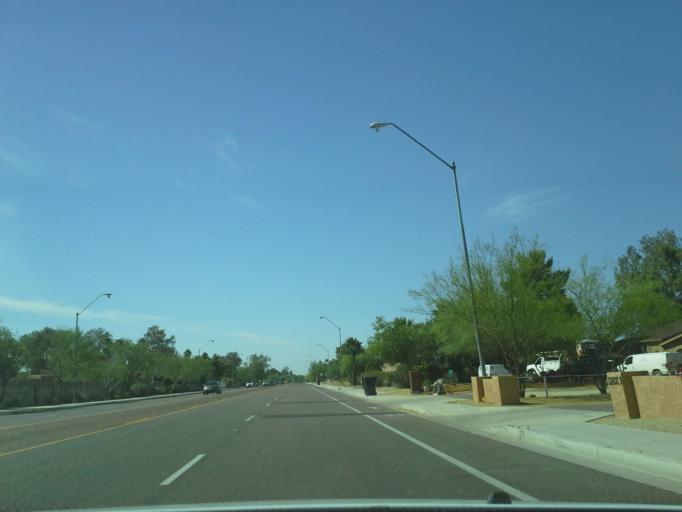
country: US
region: Arizona
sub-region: Maricopa County
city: Paradise Valley
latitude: 33.6099
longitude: -111.9086
